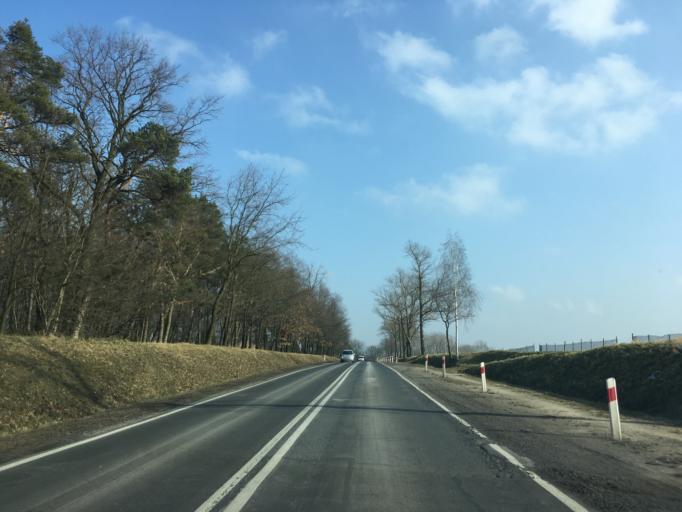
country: PL
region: Lower Silesian Voivodeship
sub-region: Powiat legnicki
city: Chojnow
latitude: 51.2657
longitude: 15.9361
